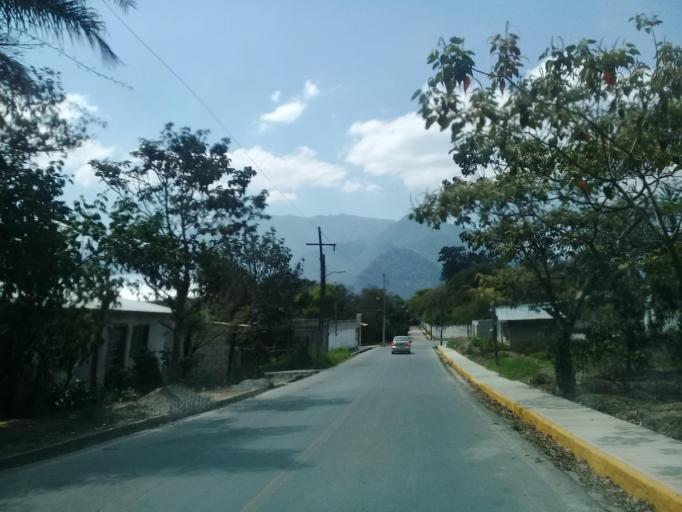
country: MX
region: Veracruz
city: Jalapilla
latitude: 18.8145
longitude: -97.0635
